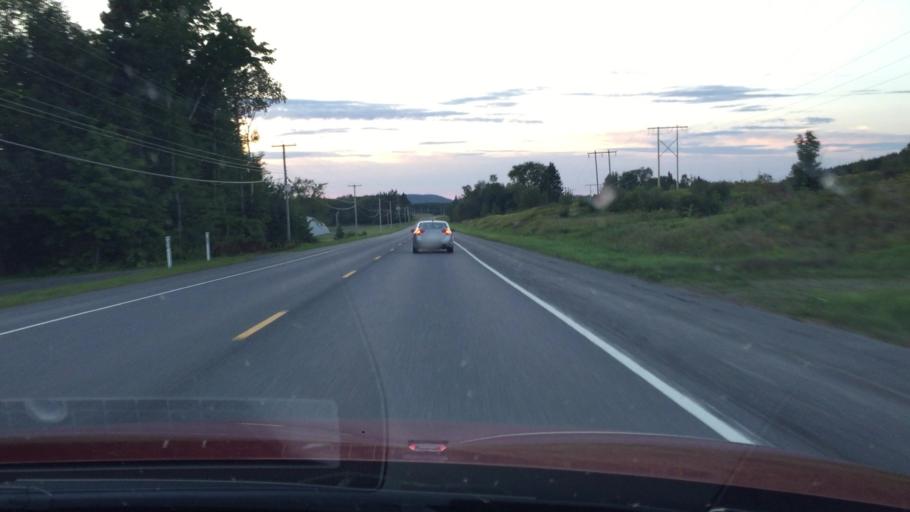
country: US
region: Maine
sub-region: Aroostook County
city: Easton
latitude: 46.4580
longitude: -67.8586
